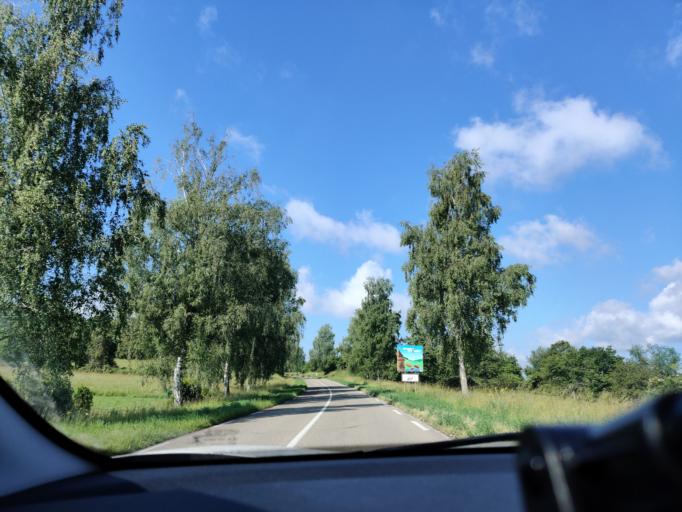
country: FR
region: Lorraine
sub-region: Departement de la Moselle
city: Sarreinsming
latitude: 49.1373
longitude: 7.1221
